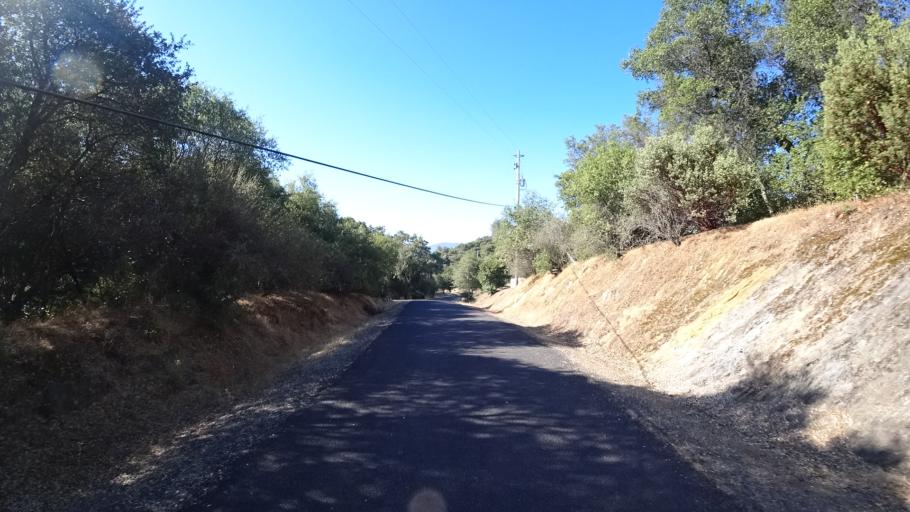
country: US
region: California
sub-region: Calaveras County
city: San Andreas
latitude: 38.2534
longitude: -120.7061
